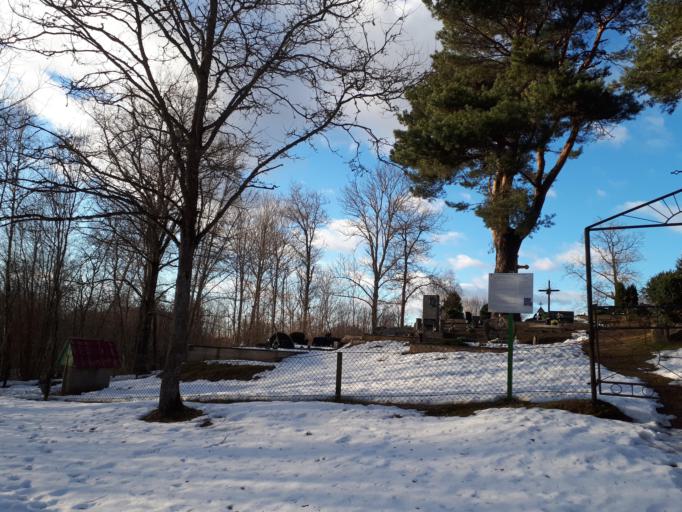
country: LT
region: Alytaus apskritis
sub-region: Alytus
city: Alytus
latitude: 54.4136
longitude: 24.1219
